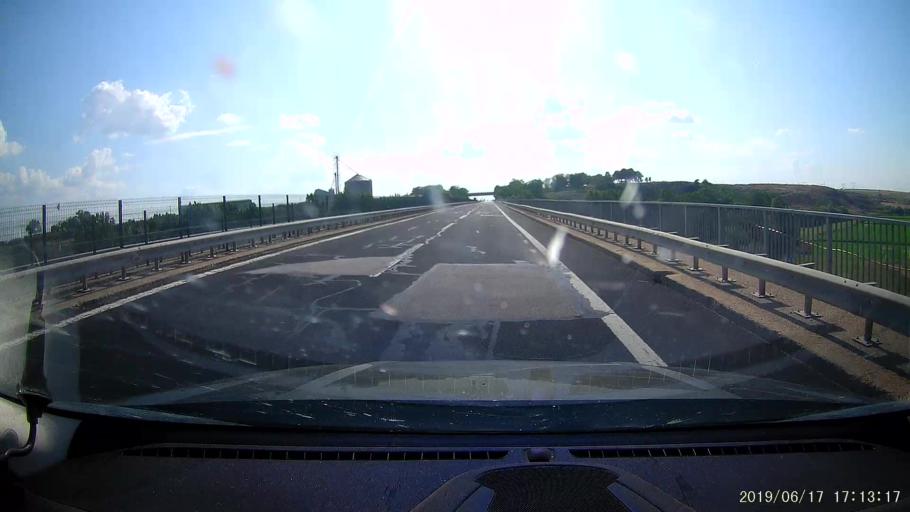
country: TR
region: Edirne
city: Edirne
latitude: 41.7010
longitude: 26.5433
